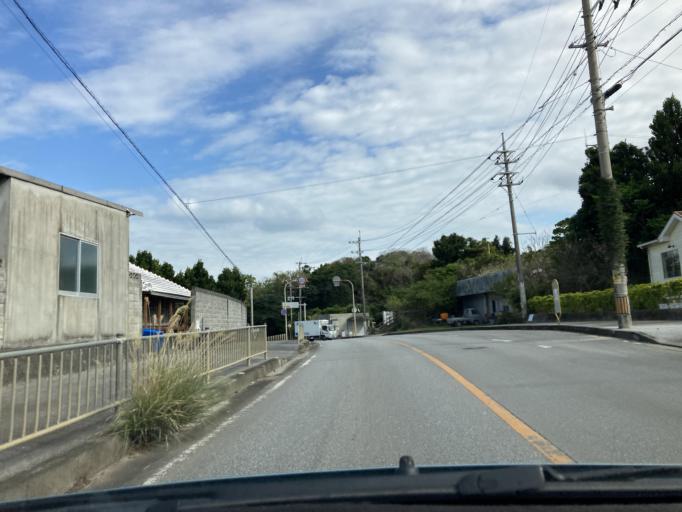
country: JP
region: Okinawa
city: Nago
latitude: 26.6963
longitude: 127.9434
